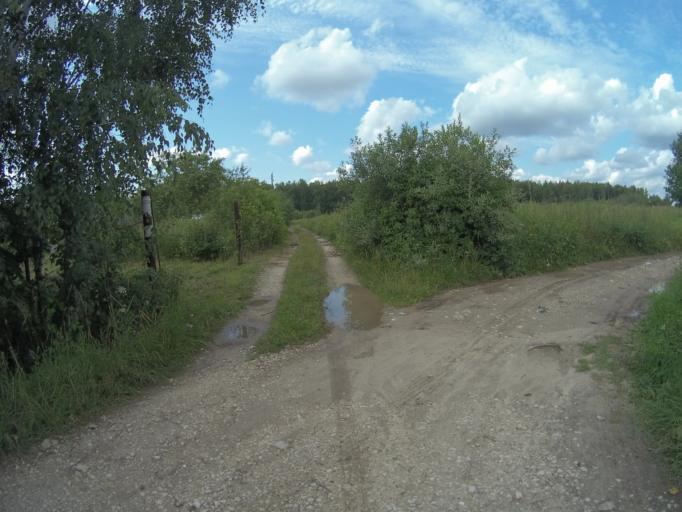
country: RU
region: Vladimir
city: Orgtrud
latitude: 56.2459
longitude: 40.6944
